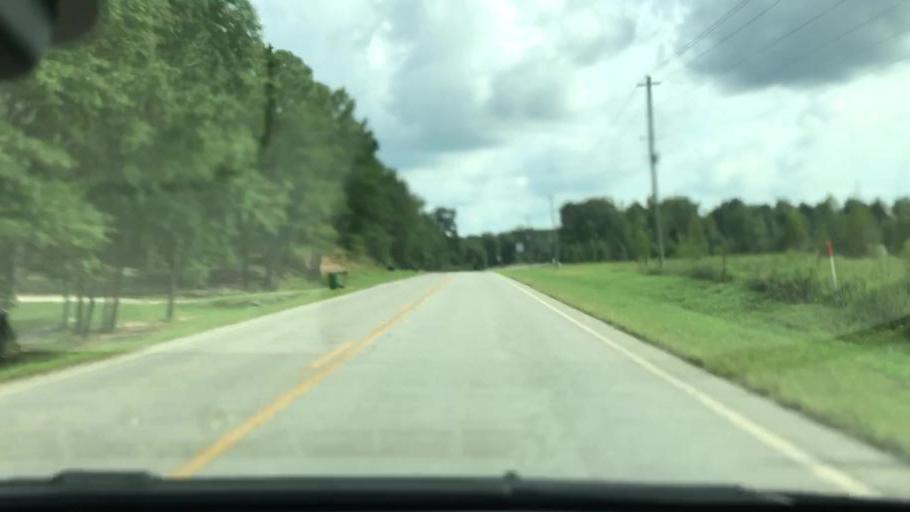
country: US
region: Georgia
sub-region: Clay County
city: Fort Gaines
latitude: 31.6482
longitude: -85.0453
